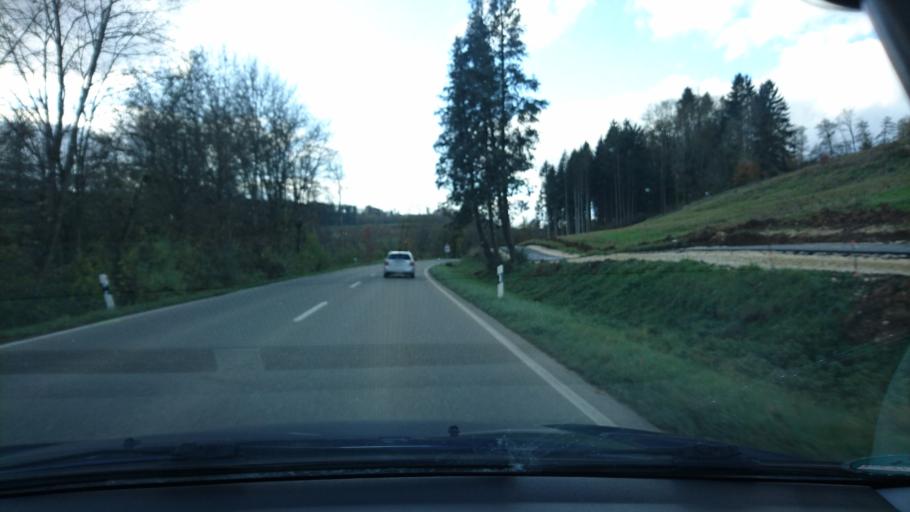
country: DE
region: Baden-Wuerttemberg
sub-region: Regierungsbezirk Stuttgart
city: Goggingen
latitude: 48.8490
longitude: 9.9026
